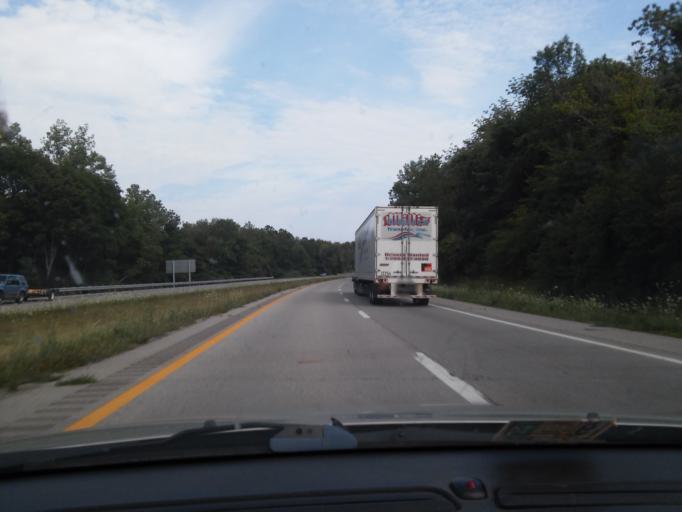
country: US
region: Ohio
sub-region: Ross County
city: North Fork Village
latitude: 39.3739
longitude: -83.0316
